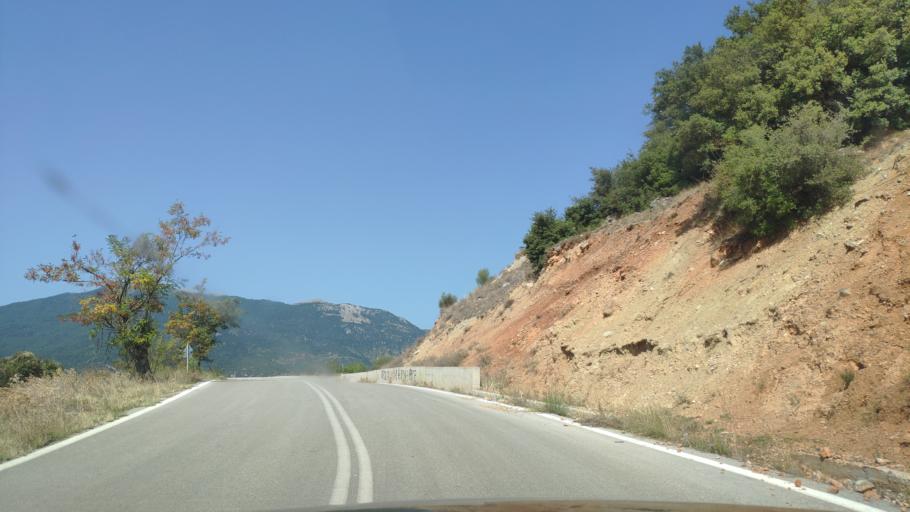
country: GR
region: West Greece
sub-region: Nomos Achaias
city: Aiyira
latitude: 37.9224
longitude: 22.3390
